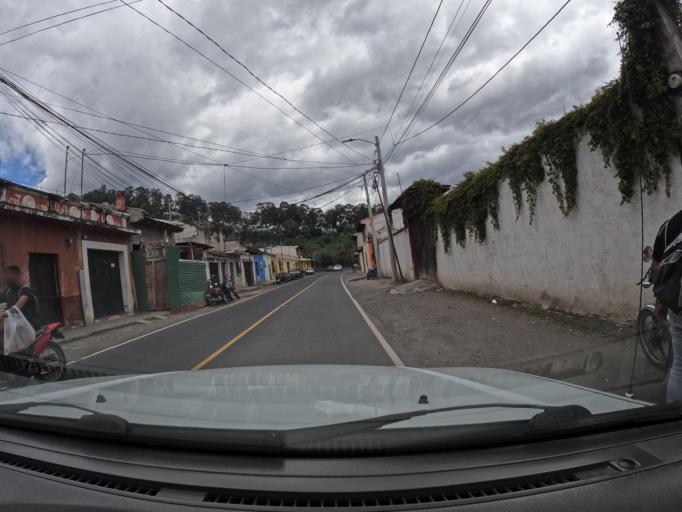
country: GT
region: Sacatepequez
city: Antigua Guatemala
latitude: 14.5699
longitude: -90.7357
